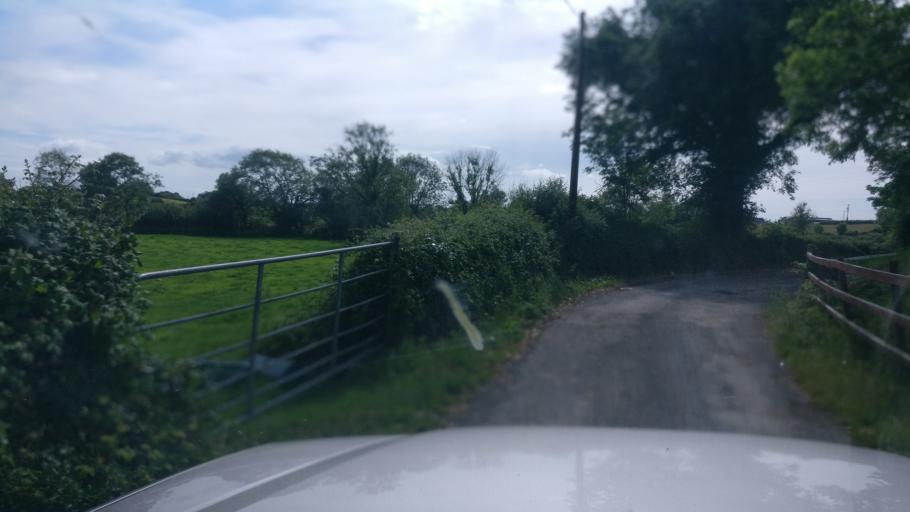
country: IE
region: Connaught
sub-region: County Galway
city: Gort
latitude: 53.0708
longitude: -8.7649
